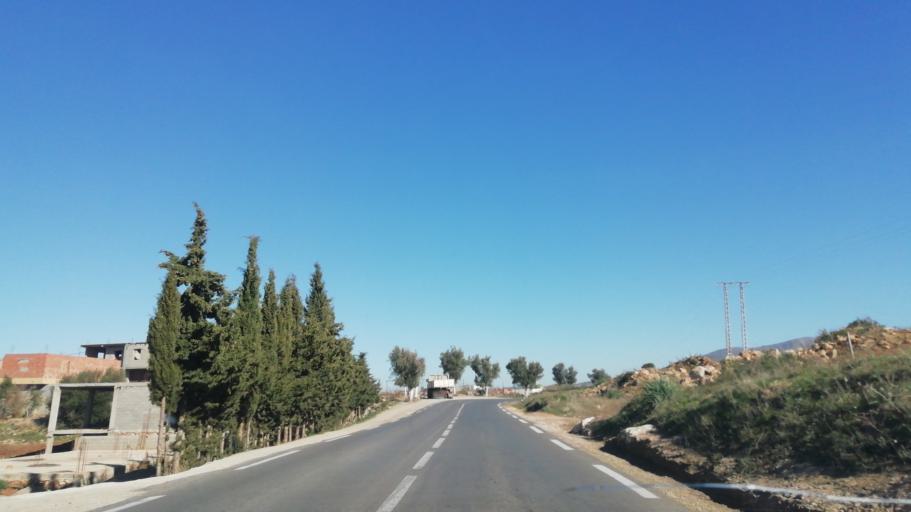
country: DZ
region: Tlemcen
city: Beni Mester
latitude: 34.8409
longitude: -1.4805
